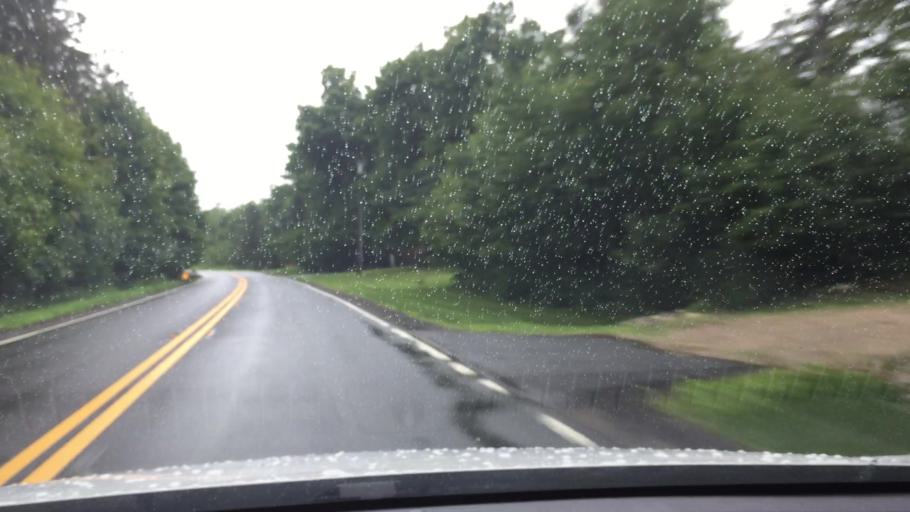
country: US
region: Massachusetts
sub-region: Berkshire County
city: Hinsdale
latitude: 42.3706
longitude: -73.1461
